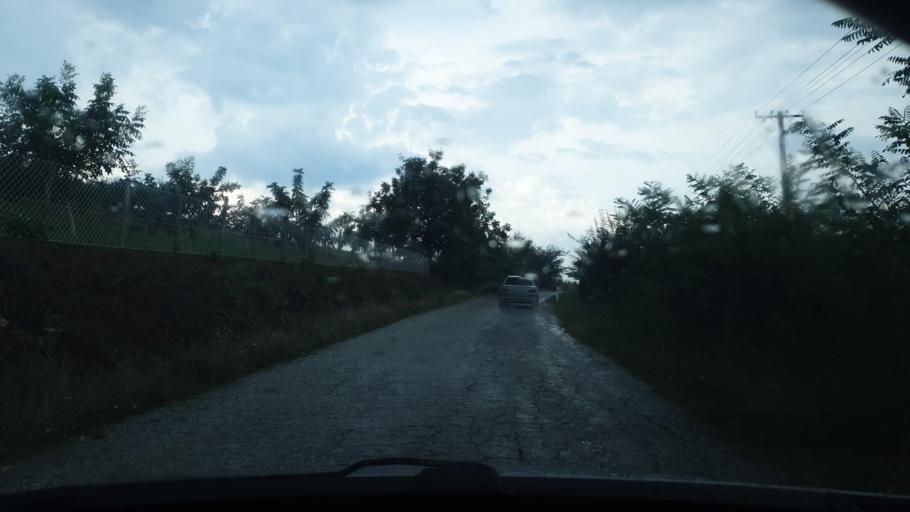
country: RS
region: Central Serbia
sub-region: Sumadijski Okrug
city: Kragujevac
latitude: 44.0726
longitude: 20.7884
